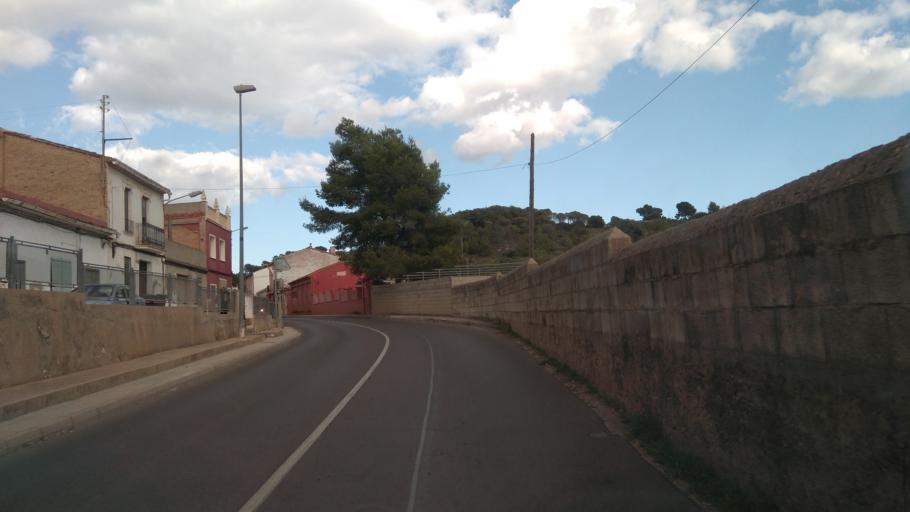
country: ES
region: Valencia
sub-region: Provincia de Valencia
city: Alzira
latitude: 39.1506
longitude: -0.4189
